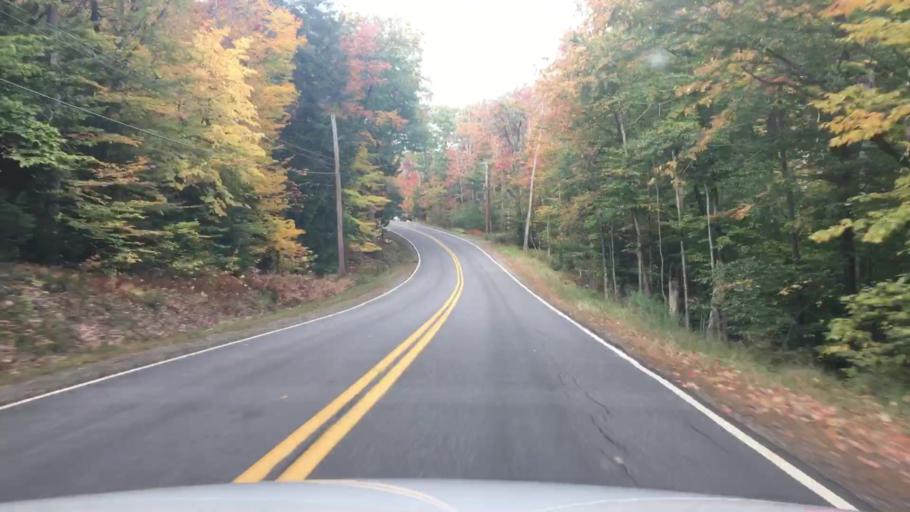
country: US
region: Maine
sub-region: Knox County
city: Hope
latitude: 44.2413
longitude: -69.1143
